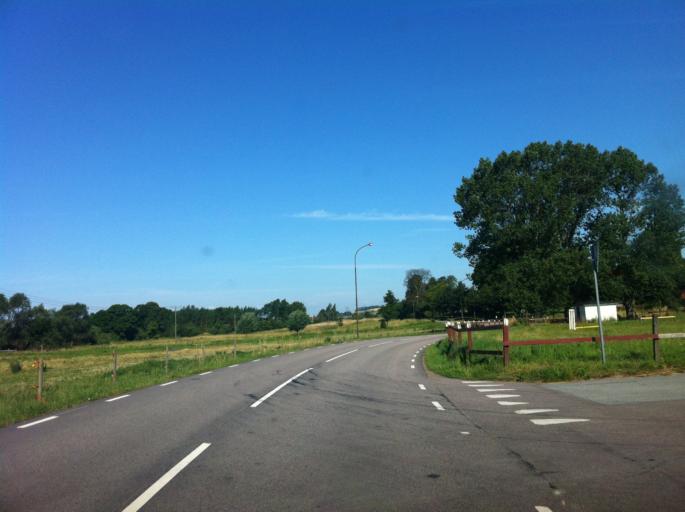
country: SE
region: Skane
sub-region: Landskrona
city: Asmundtorp
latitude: 55.8838
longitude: 12.9906
